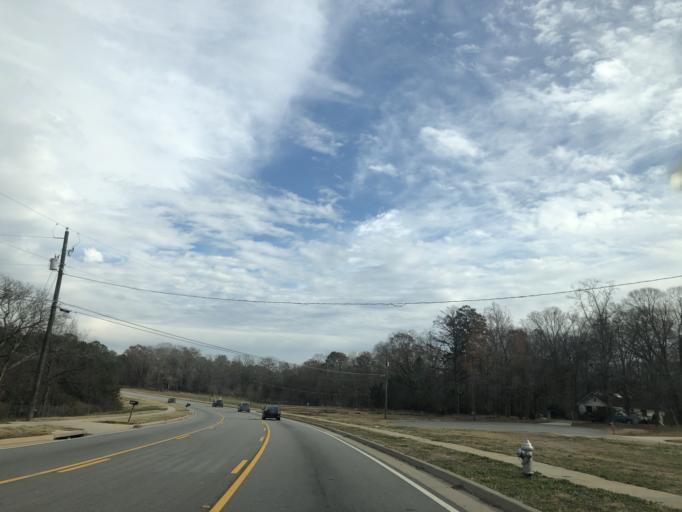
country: US
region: Georgia
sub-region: Clayton County
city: Conley
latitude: 33.6269
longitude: -84.2775
